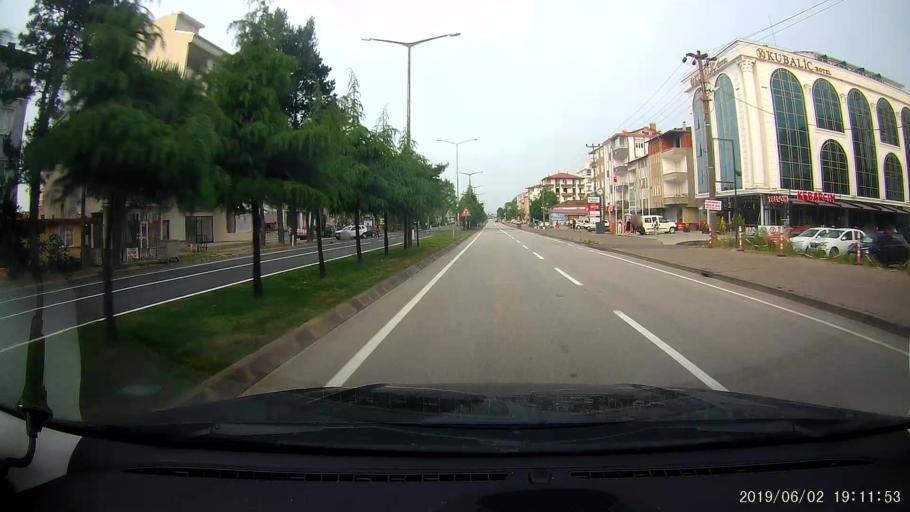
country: TR
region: Ordu
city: Gulyali
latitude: 40.9666
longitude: 38.0598
